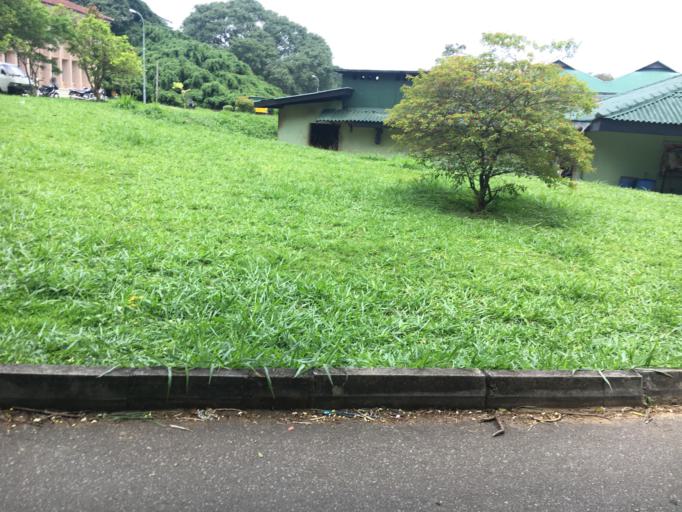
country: LK
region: Central
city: Kandy
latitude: 7.2563
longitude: 80.5965
